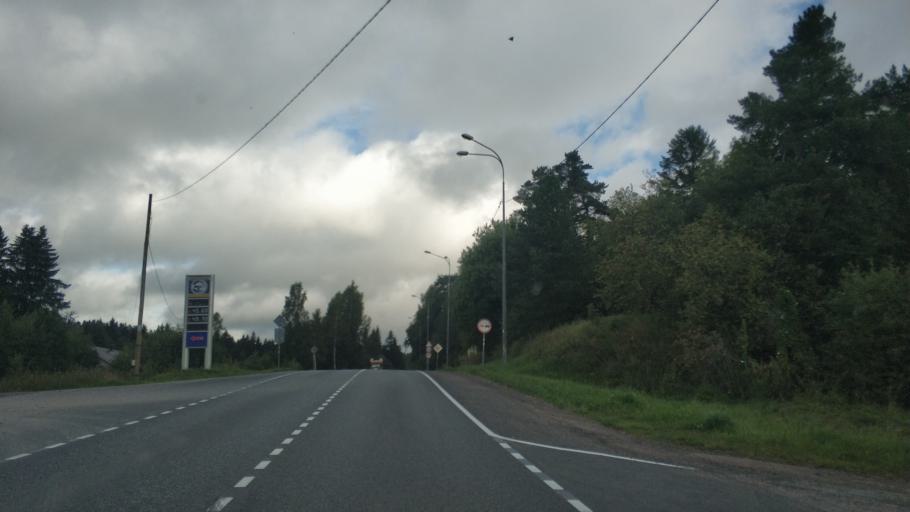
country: RU
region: Republic of Karelia
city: Khelyulya
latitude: 61.7532
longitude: 30.6590
